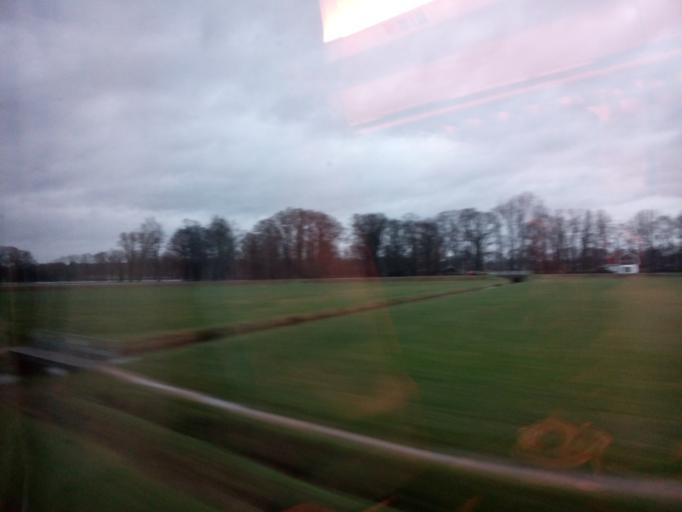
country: NL
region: Overijssel
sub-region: Gemeente Borne
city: Borne
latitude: 52.3176
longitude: 6.7164
